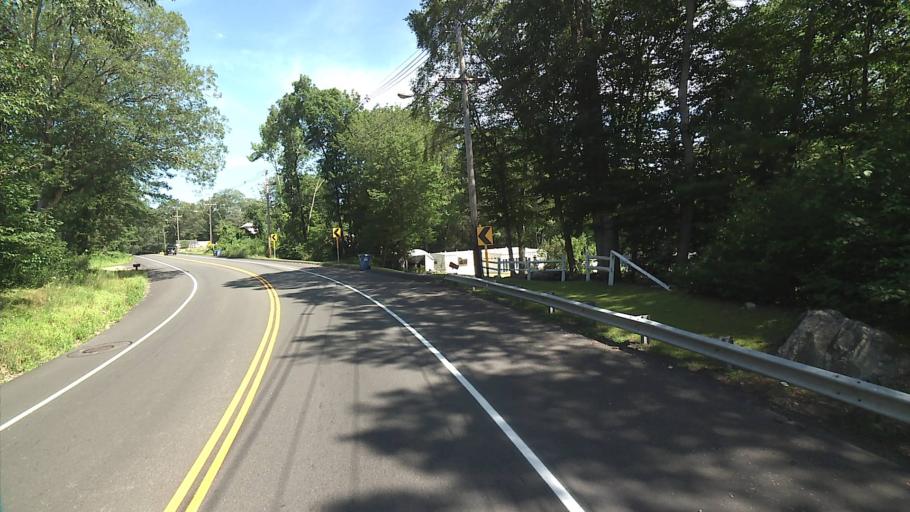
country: US
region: Connecticut
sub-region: New London County
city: Lisbon
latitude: 41.5786
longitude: -72.0446
